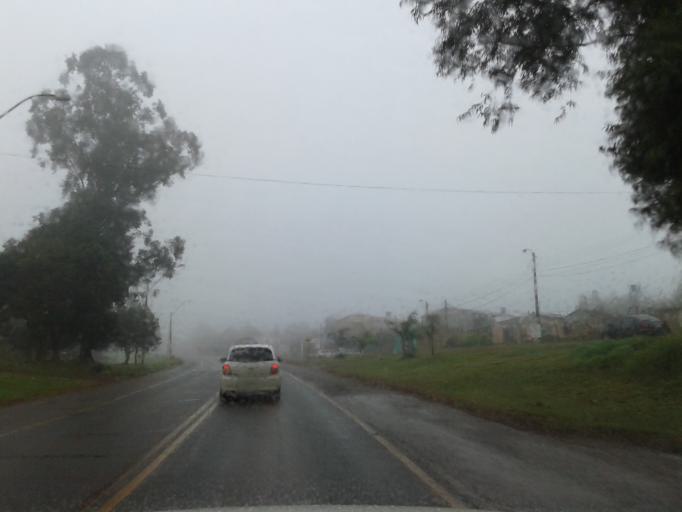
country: PY
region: Itapua
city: Arquitecto Tomas Romero Pereira
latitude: -26.5435
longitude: -55.2559
